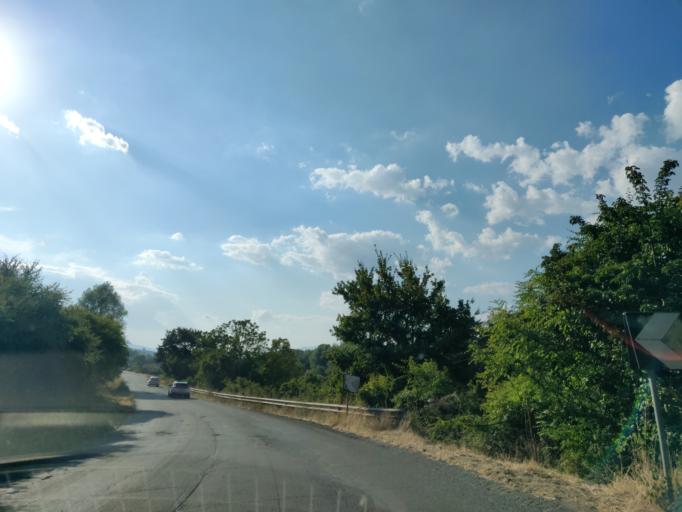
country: IT
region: Latium
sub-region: Provincia di Viterbo
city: Acquapendente
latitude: 42.7607
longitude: 11.8632
